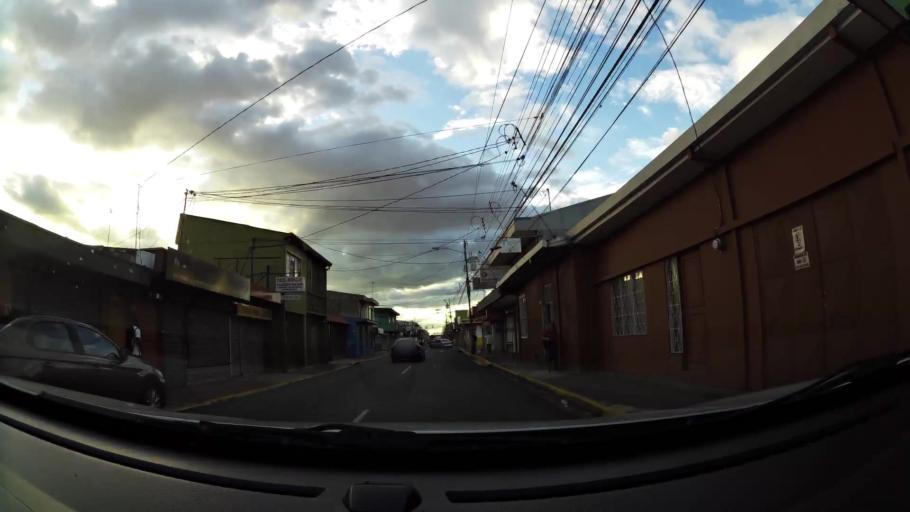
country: CR
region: Heredia
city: Heredia
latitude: 9.9974
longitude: -84.1196
